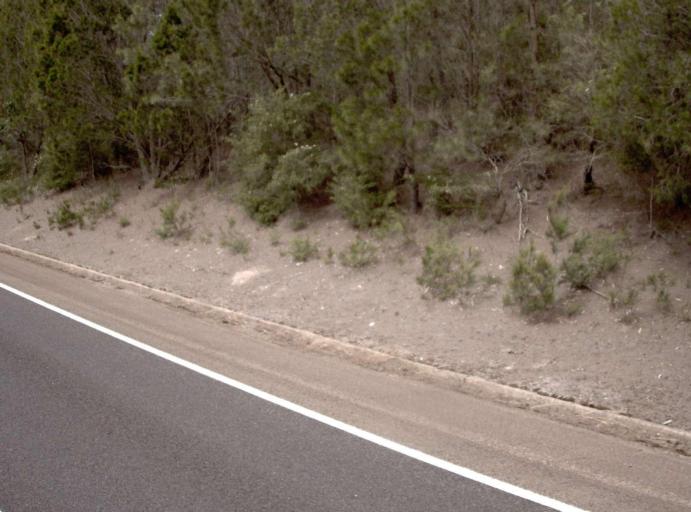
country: AU
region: New South Wales
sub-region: Bega Valley
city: Eden
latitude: -37.4136
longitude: 149.6544
